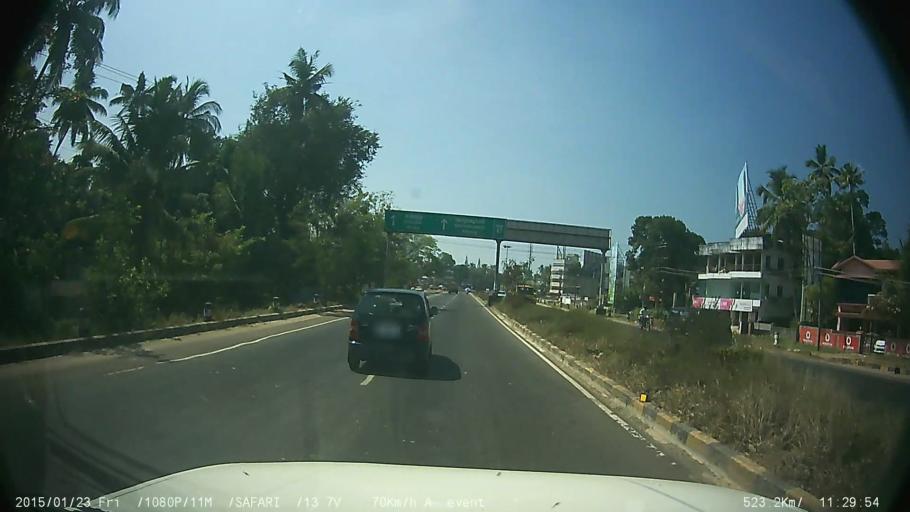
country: IN
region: Kerala
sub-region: Alappuzha
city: Arukutti
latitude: 9.8799
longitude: 76.3052
